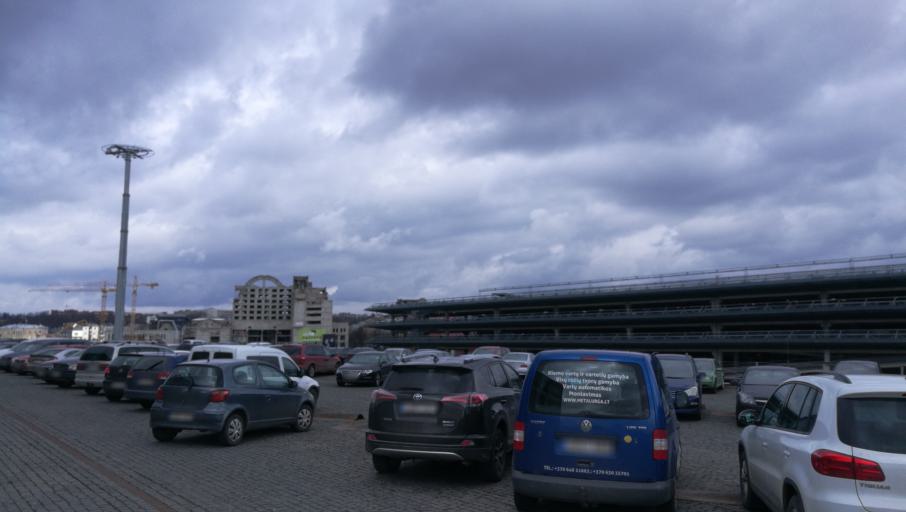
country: LT
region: Kauno apskritis
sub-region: Kaunas
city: Aleksotas
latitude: 54.8902
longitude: 23.9159
